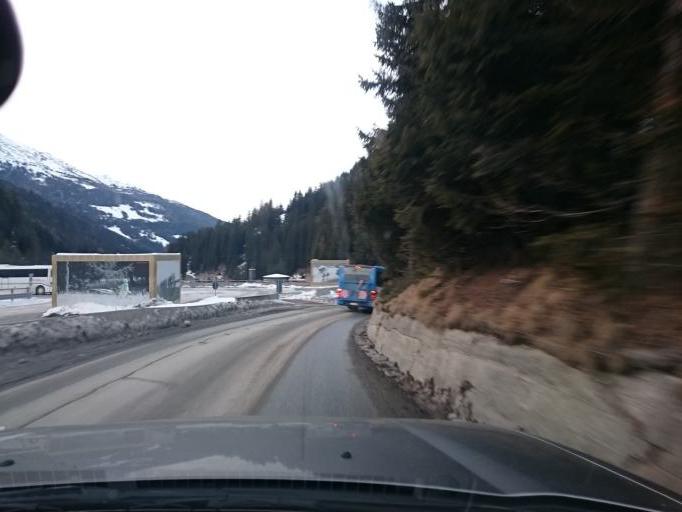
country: IT
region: Lombardy
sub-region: Provincia di Sondrio
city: Sant'Antonio
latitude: 46.4170
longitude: 10.4849
